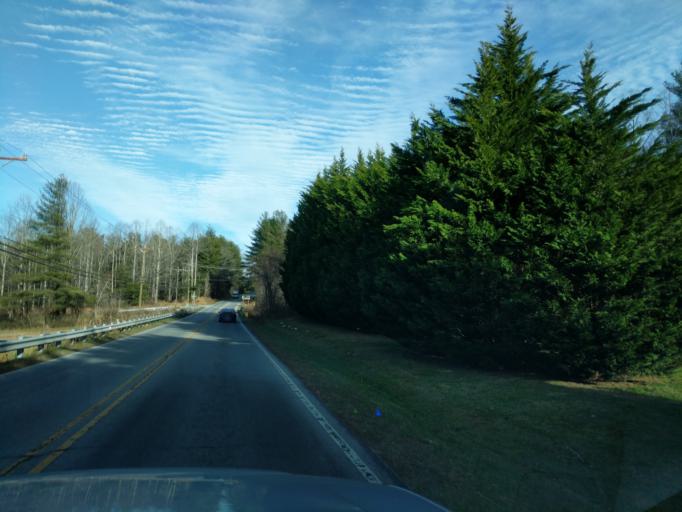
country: US
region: North Carolina
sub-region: Henderson County
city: Fruitland
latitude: 35.3738
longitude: -82.3970
